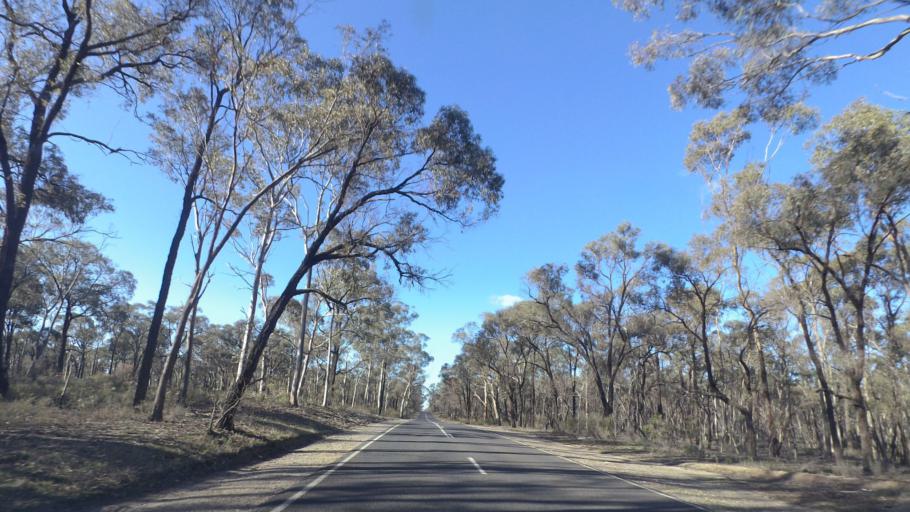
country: AU
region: Victoria
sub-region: Greater Bendigo
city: Epsom
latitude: -36.6657
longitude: 144.4384
